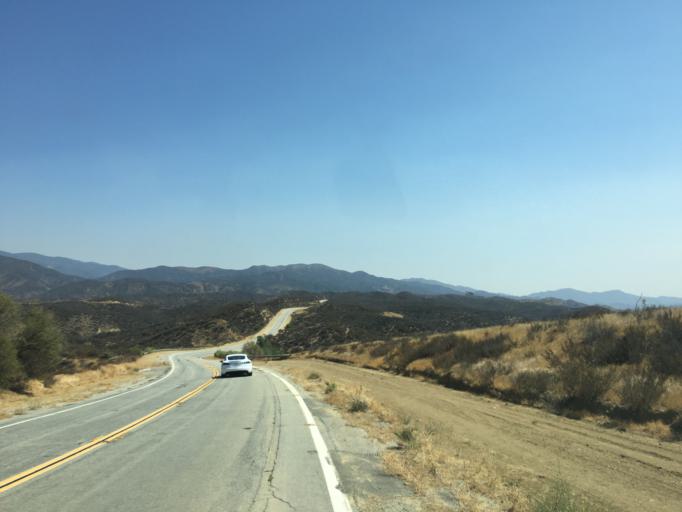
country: US
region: California
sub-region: Los Angeles County
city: Castaic
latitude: 34.5200
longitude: -118.5788
